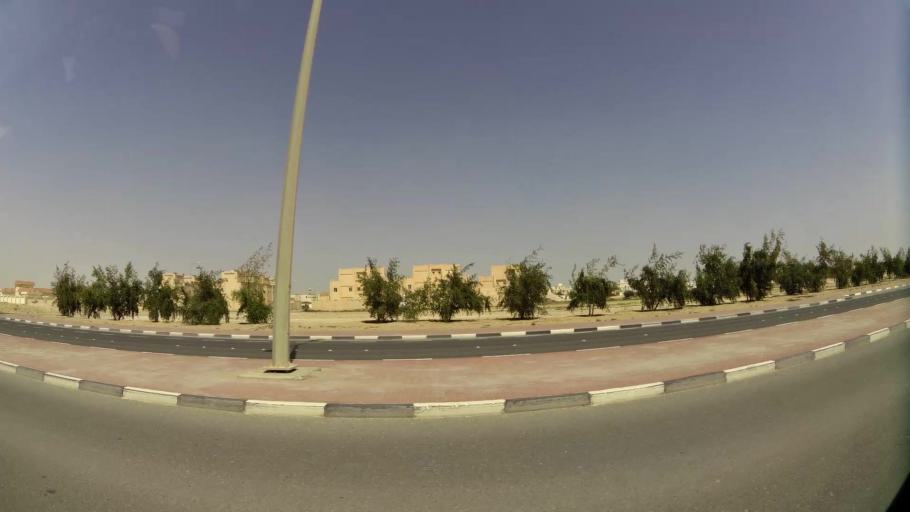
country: QA
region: Baladiyat Umm Salal
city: Umm Salal Muhammad
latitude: 25.3898
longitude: 51.4218
